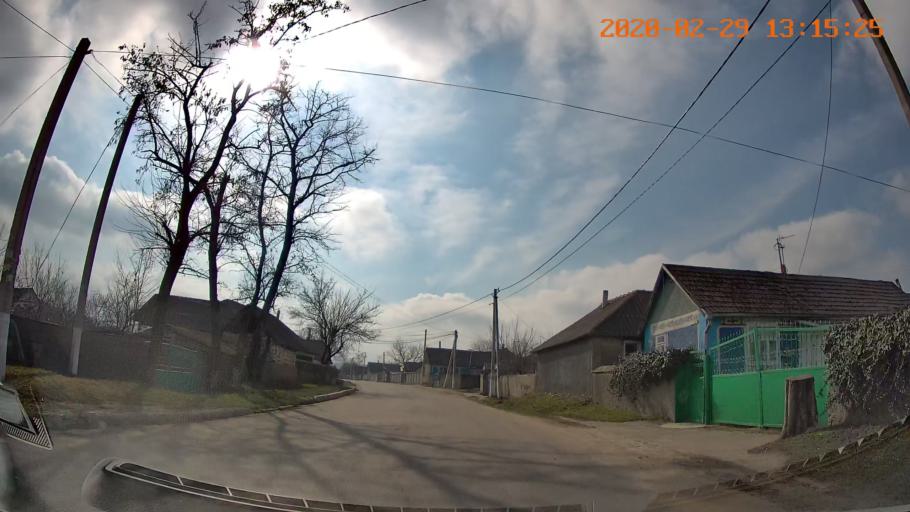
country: MD
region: Telenesti
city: Camenca
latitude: 48.0100
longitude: 28.6694
